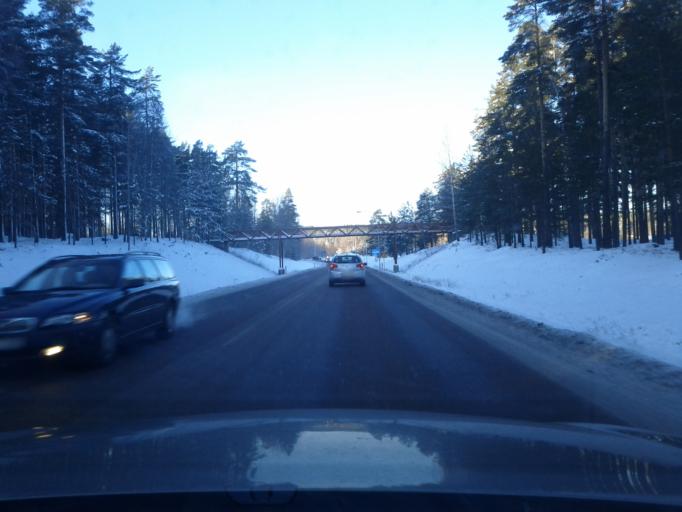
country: SE
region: Dalarna
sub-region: Faluns Kommun
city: Falun
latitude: 60.6168
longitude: 15.6493
